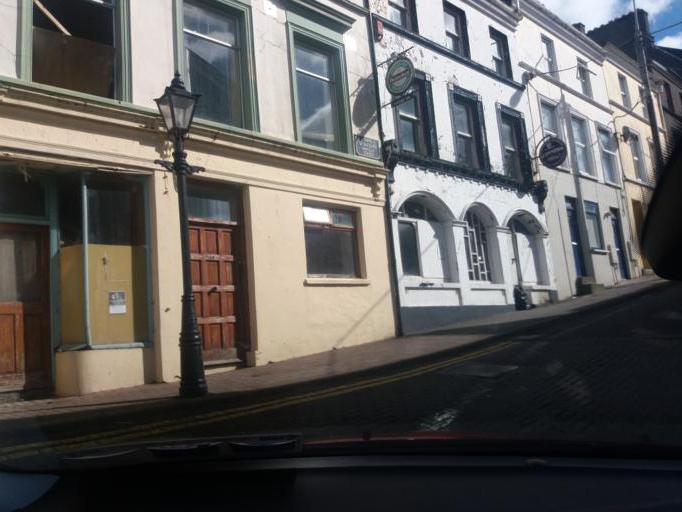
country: IE
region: Munster
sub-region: County Cork
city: Cobh
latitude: 51.8508
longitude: -8.2945
